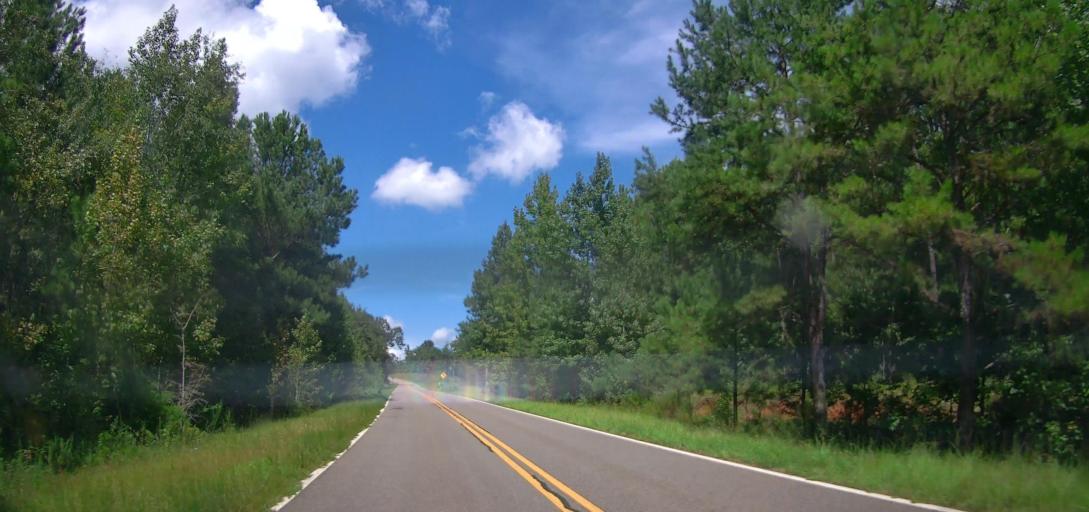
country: US
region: Georgia
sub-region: Peach County
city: Fort Valley
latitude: 32.5108
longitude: -83.8284
